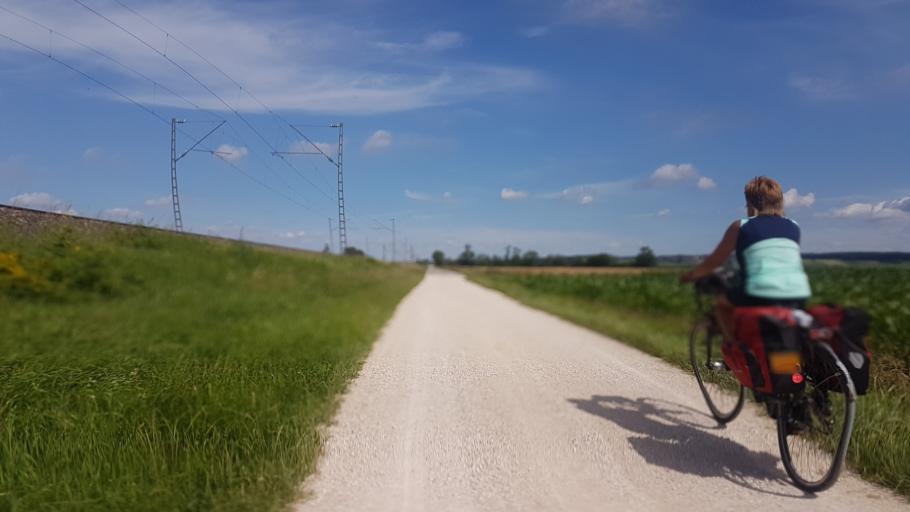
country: DE
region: Bavaria
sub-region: Regierungsbezirk Mittelfranken
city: Markt Berolzheim
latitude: 49.0287
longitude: 10.8448
